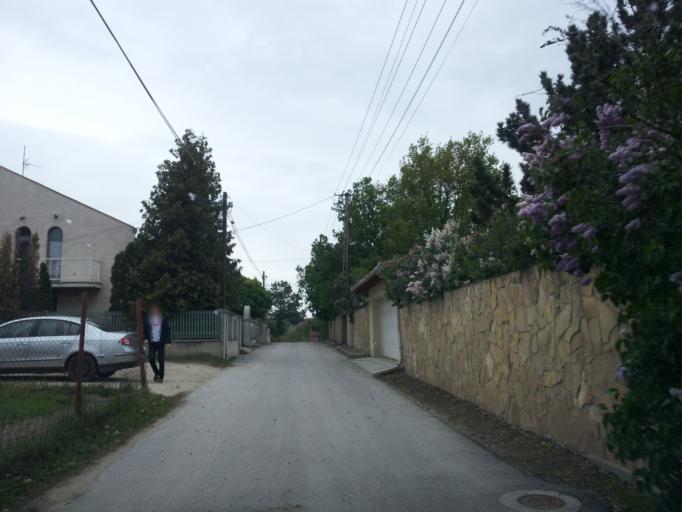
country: HU
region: Pest
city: Erd
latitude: 47.4042
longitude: 18.9266
